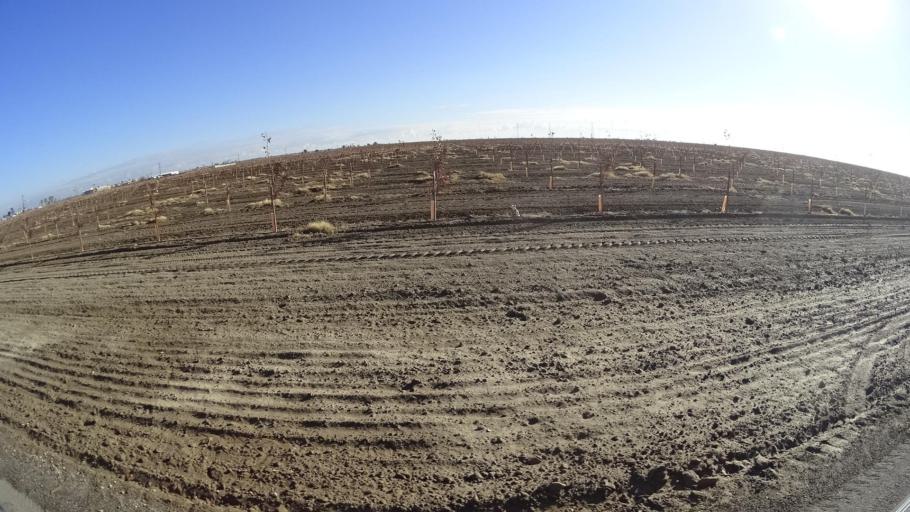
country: US
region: California
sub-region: Kern County
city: Delano
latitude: 35.7594
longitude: -119.3119
